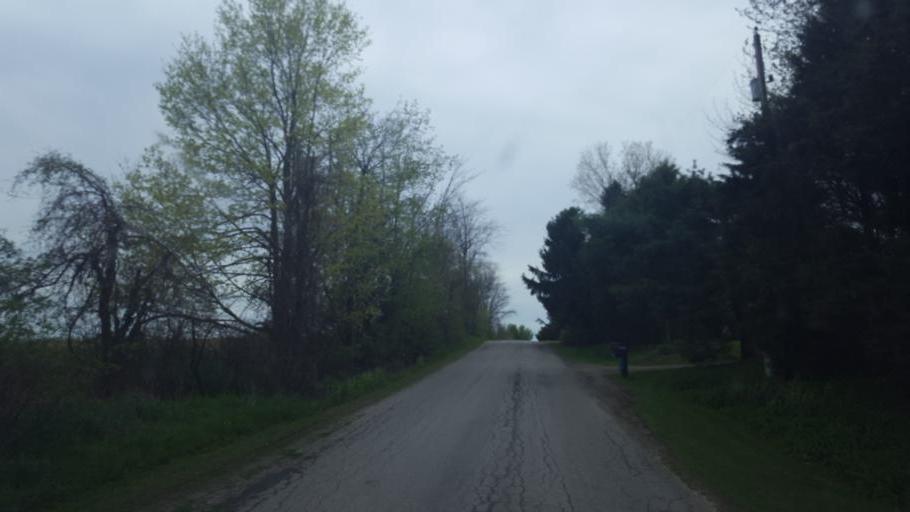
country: US
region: Ohio
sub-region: Richland County
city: Lexington
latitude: 40.6853
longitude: -82.6894
